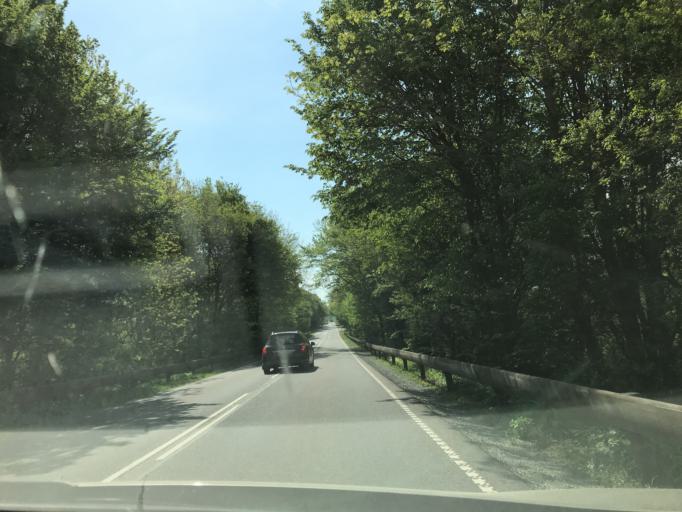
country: DK
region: South Denmark
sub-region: Middelfart Kommune
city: Ejby
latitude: 55.3732
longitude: 9.9205
